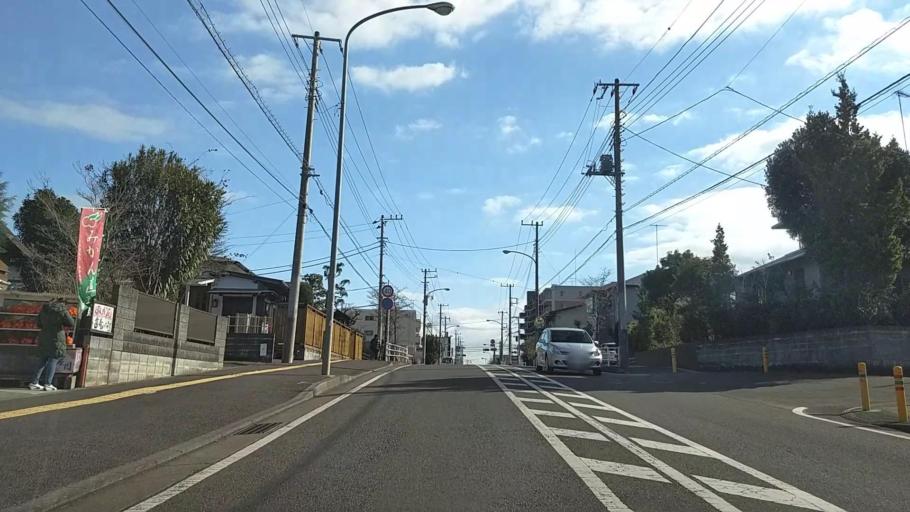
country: JP
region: Kanagawa
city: Isehara
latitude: 35.4002
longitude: 139.3154
